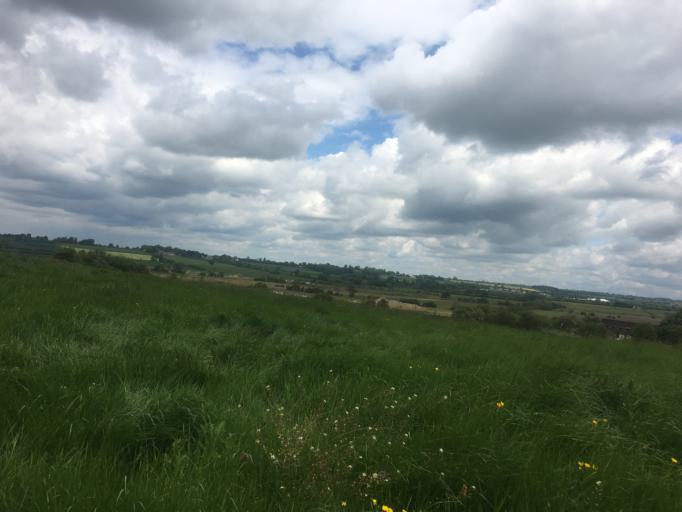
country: GB
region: England
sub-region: Warwickshire
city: Rugby
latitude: 52.3625
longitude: -1.1992
